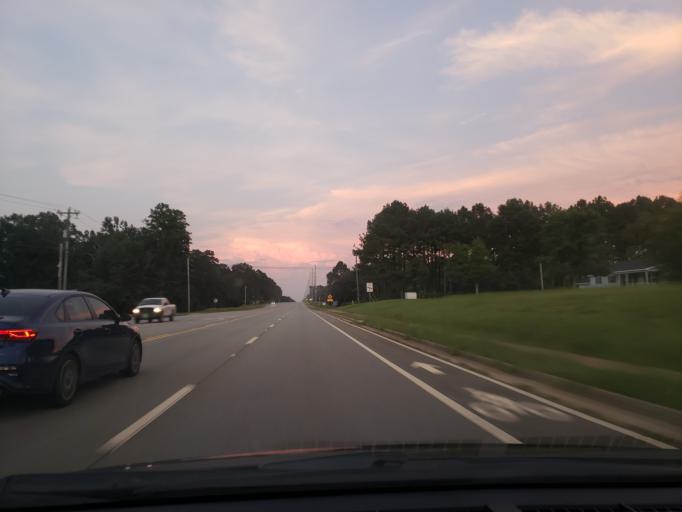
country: US
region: Georgia
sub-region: Dougherty County
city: Albany
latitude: 31.5856
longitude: -84.2846
